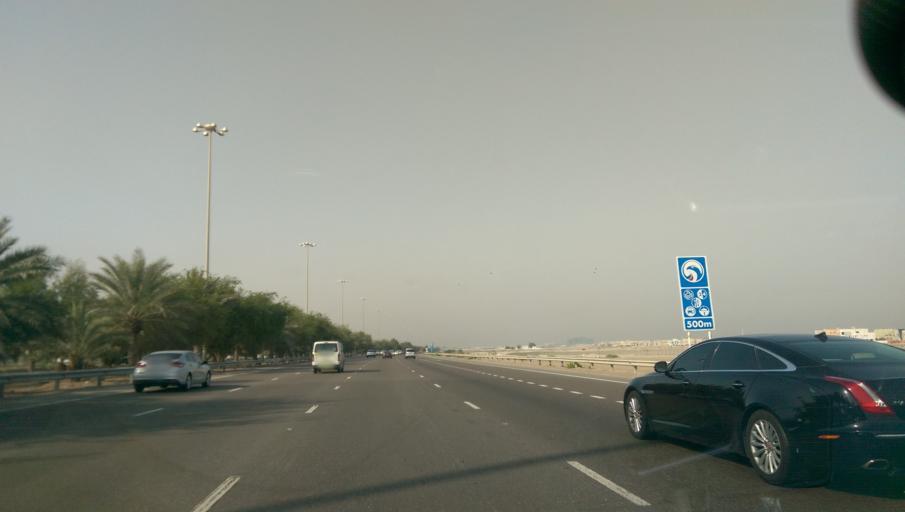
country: AE
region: Abu Dhabi
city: Abu Dhabi
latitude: 24.3642
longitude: 54.6517
